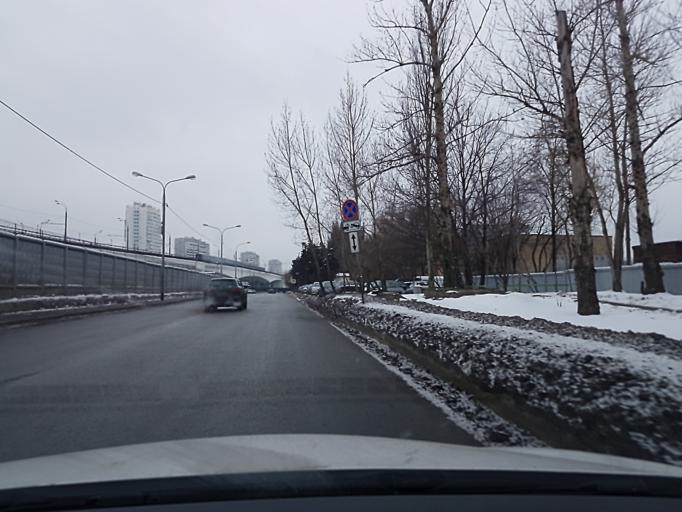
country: RU
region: Moskovskaya
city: Kozhukhovo
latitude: 55.6893
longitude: 37.6642
